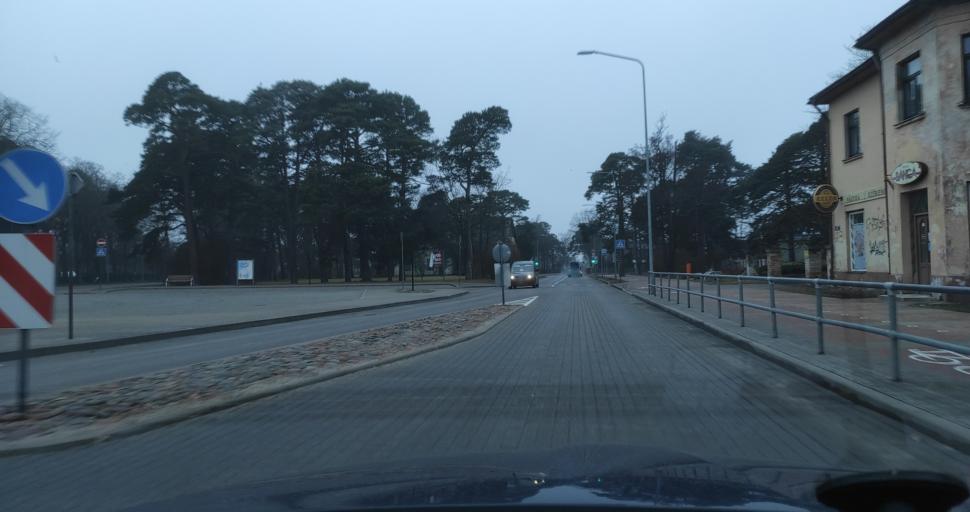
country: LV
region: Ventspils
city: Ventspils
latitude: 57.3897
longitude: 21.5496
